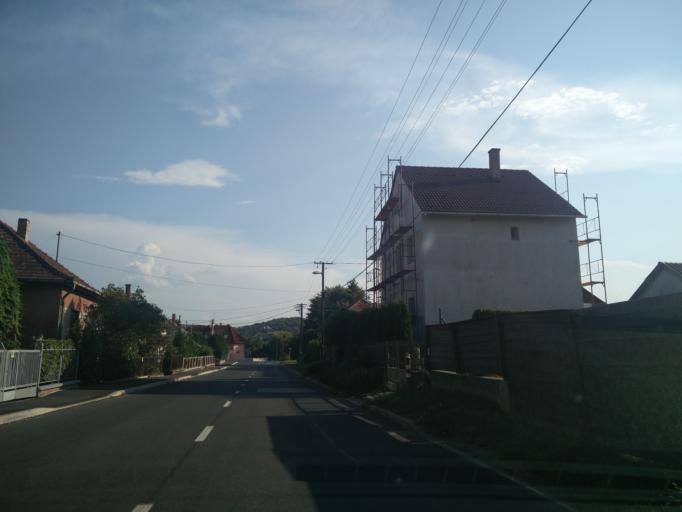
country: HU
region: Zala
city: Zalaegerszeg
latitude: 46.8632
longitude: 16.8068
